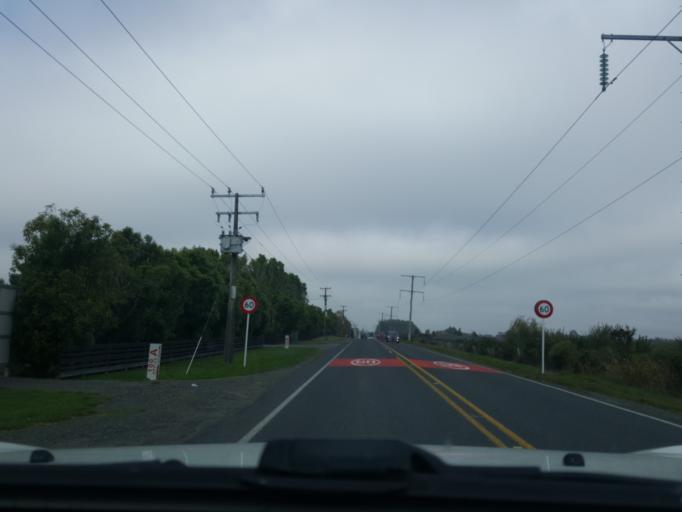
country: NZ
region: Waikato
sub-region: Hamilton City
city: Hamilton
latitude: -37.7411
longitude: 175.2898
